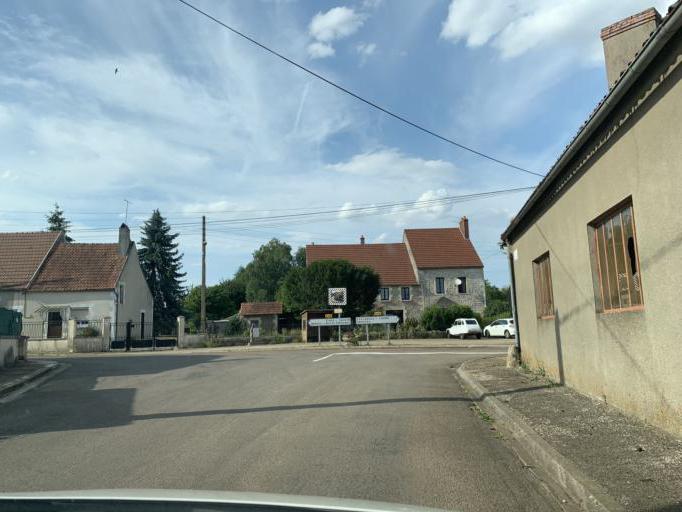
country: FR
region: Bourgogne
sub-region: Departement de l'Yonne
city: Fontenailles
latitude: 47.5200
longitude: 3.4268
